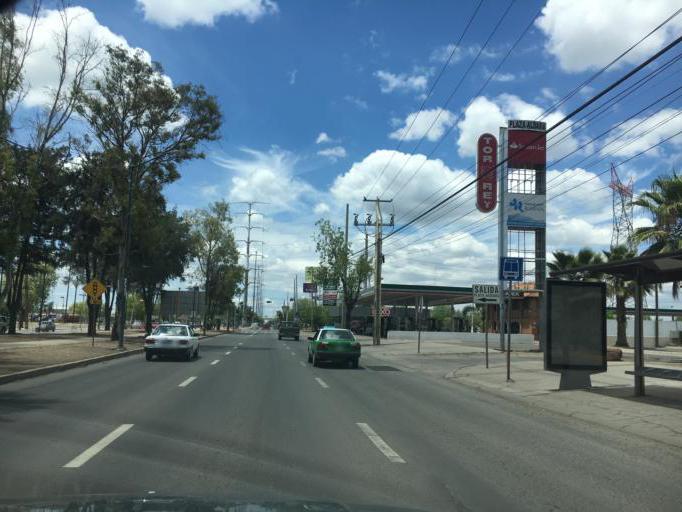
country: MX
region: Guanajuato
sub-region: Leon
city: San Jose de Duran (Los Troncoso)
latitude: 21.0761
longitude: -101.6817
